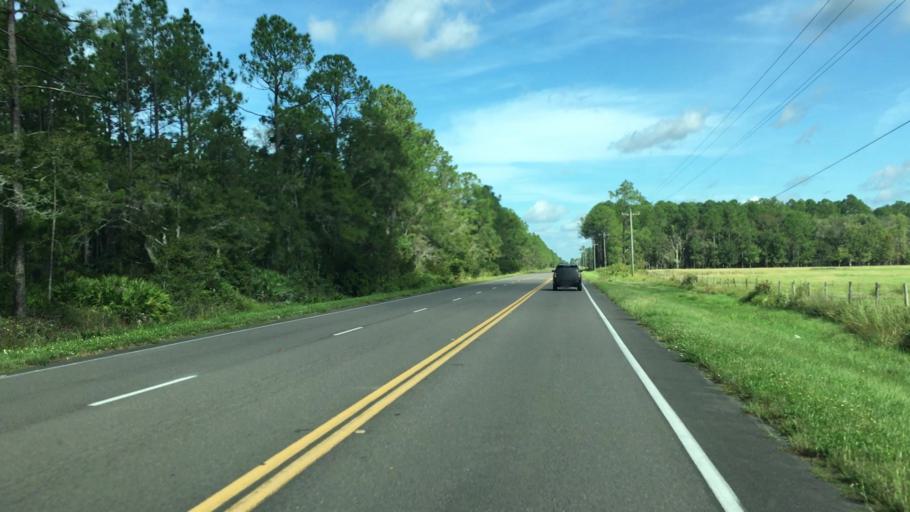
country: US
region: Florida
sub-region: Alachua County
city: Gainesville
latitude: 29.7439
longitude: -82.2770
